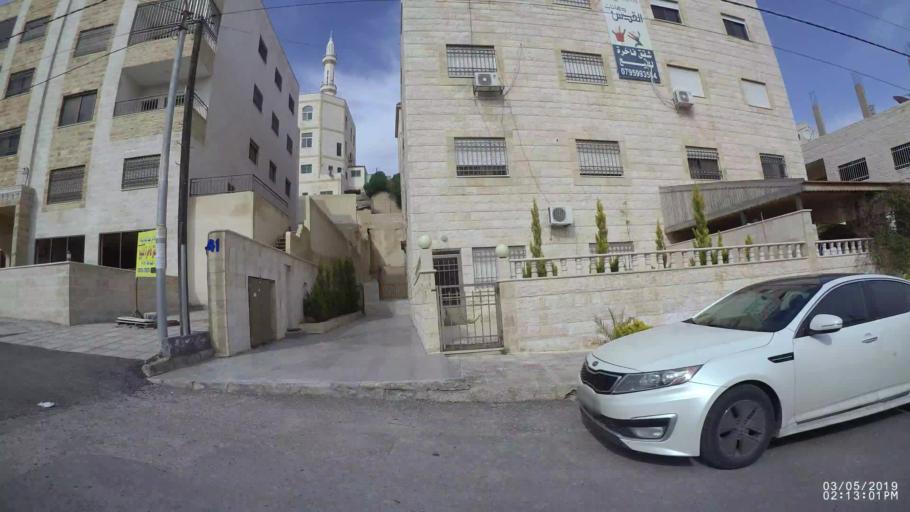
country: JO
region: Amman
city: Amman
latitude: 32.0085
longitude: 35.9419
